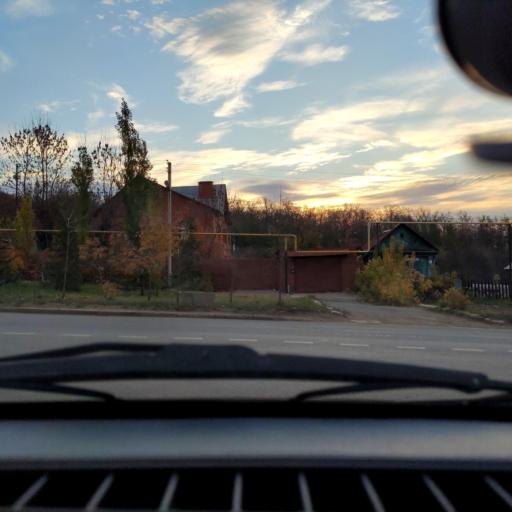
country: RU
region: Bashkortostan
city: Ufa
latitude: 54.6888
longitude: 55.9978
